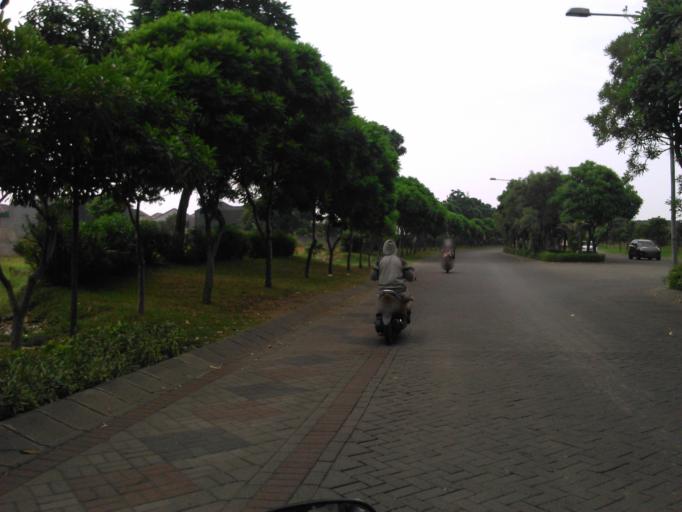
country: ID
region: East Java
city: Semampir
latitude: -7.2874
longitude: 112.7876
